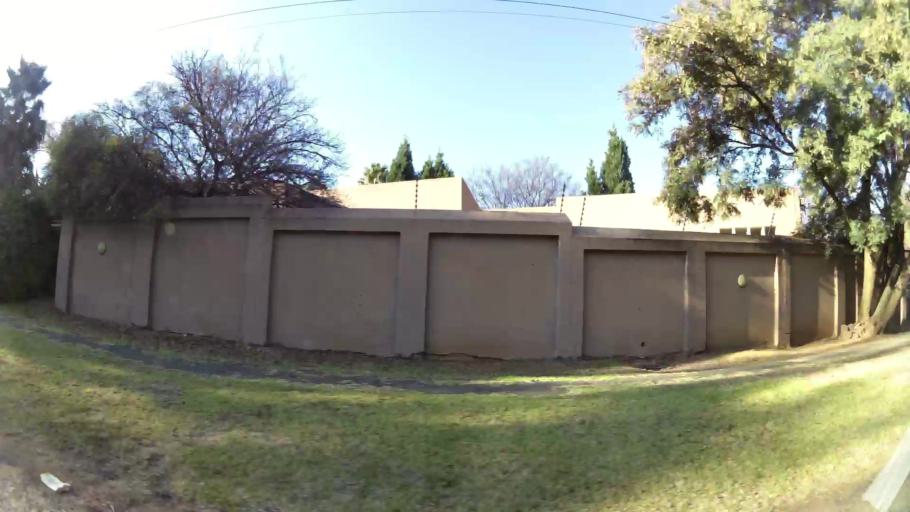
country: ZA
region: Gauteng
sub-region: City of Johannesburg Metropolitan Municipality
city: Johannesburg
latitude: -26.1378
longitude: 28.0736
